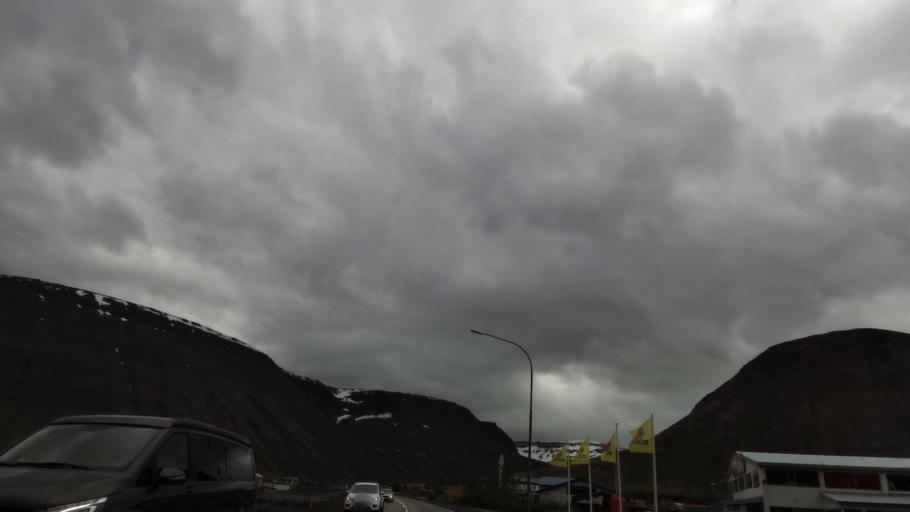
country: IS
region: Westfjords
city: Isafjoerdur
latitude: 66.0609
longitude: -23.1735
